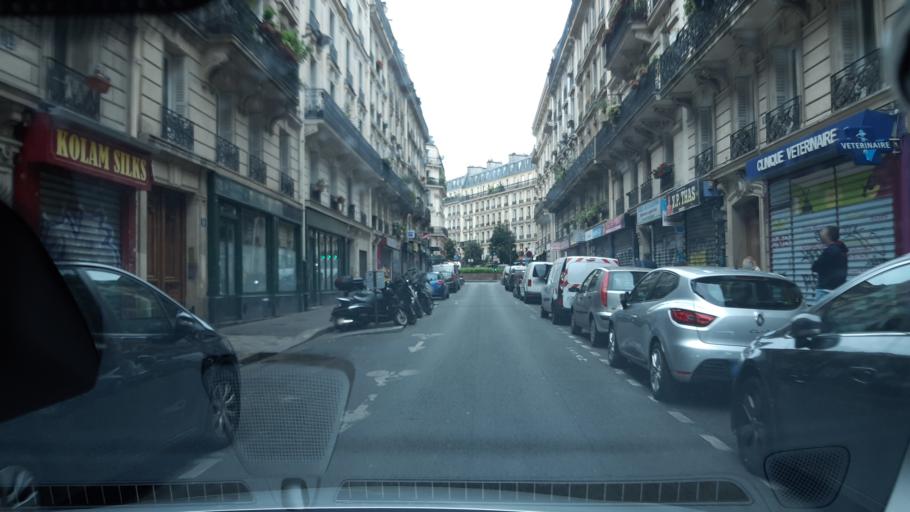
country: FR
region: Ile-de-France
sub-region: Paris
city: Saint-Ouen
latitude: 48.8834
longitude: 2.3602
